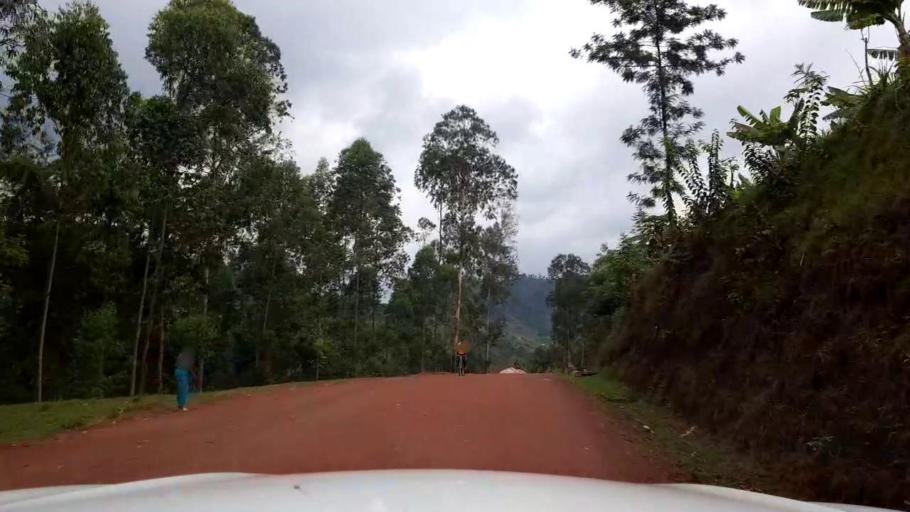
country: RW
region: Northern Province
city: Musanze
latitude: -1.6610
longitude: 29.8009
